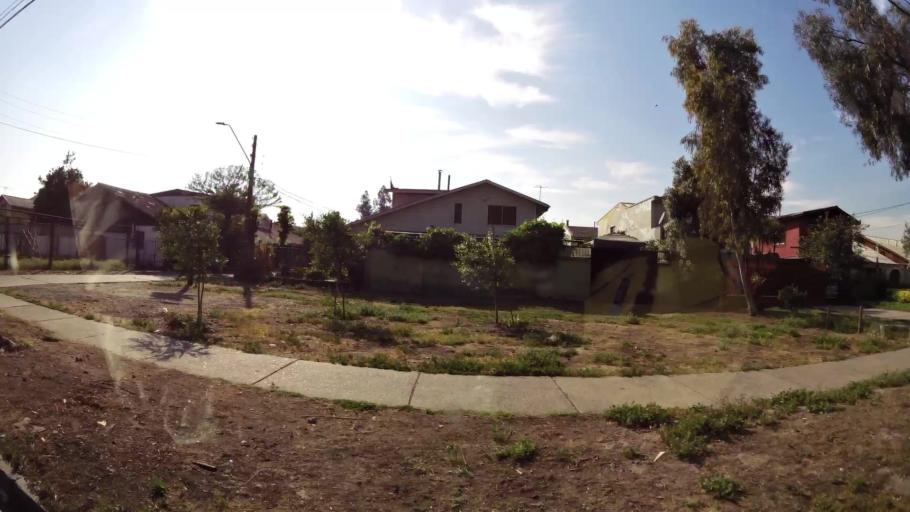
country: CL
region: Santiago Metropolitan
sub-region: Provincia de Maipo
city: San Bernardo
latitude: -33.6007
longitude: -70.7158
